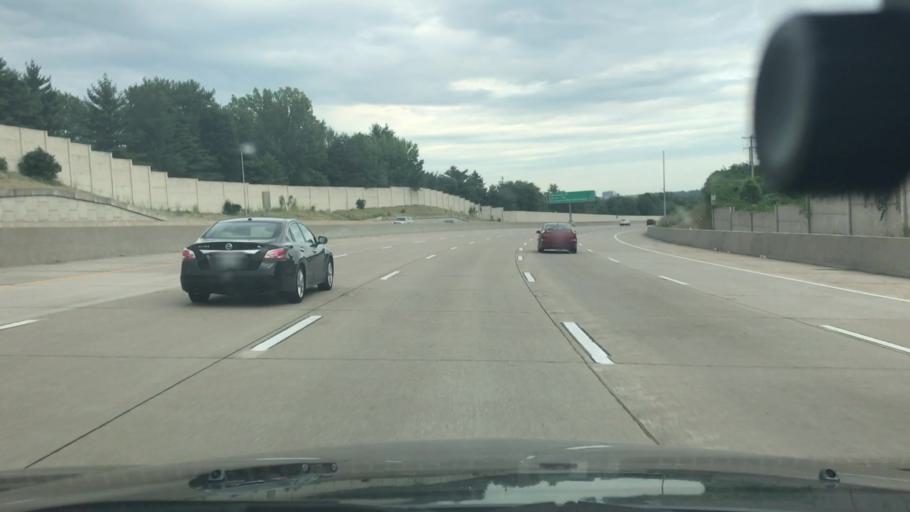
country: US
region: Missouri
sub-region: Saint Louis County
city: Maryland Heights
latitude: 38.7048
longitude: -90.4750
